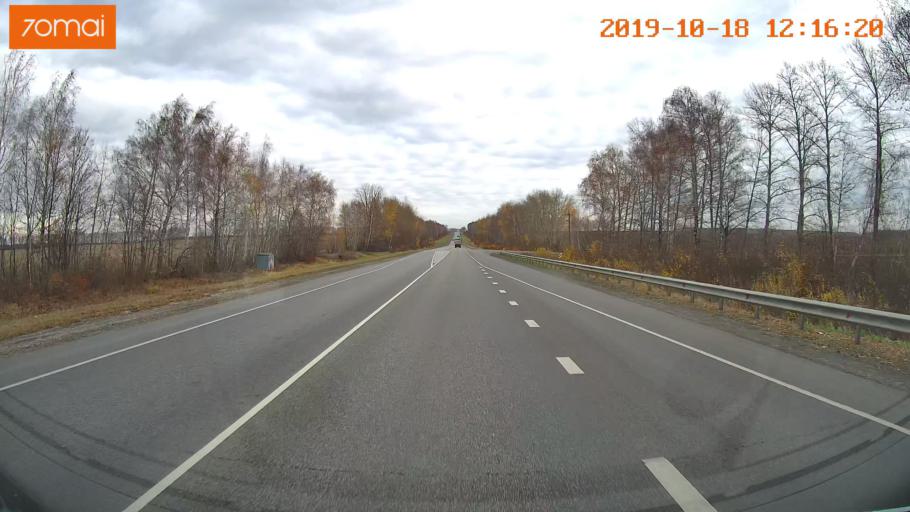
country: RU
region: Rjazan
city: Zakharovo
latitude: 54.4514
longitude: 39.4194
